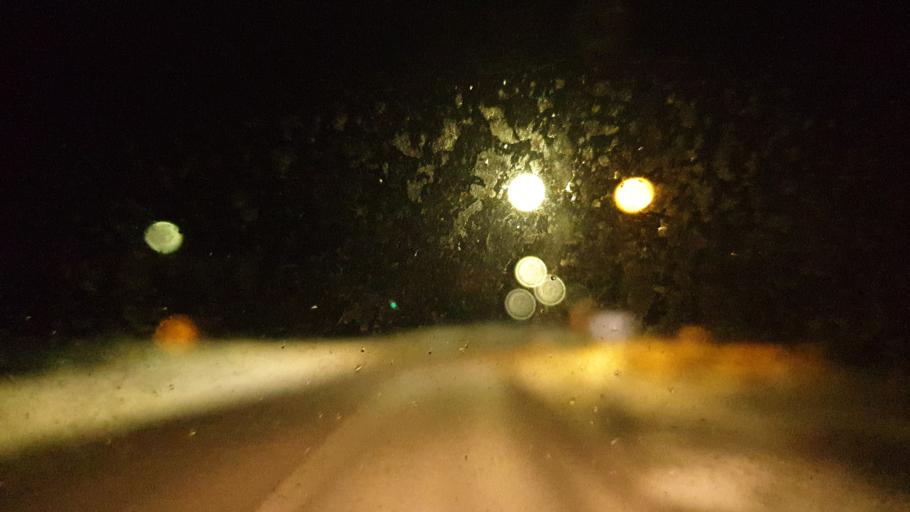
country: FI
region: Southern Savonia
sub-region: Pieksaemaeki
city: Juva
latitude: 61.8773
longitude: 27.7736
